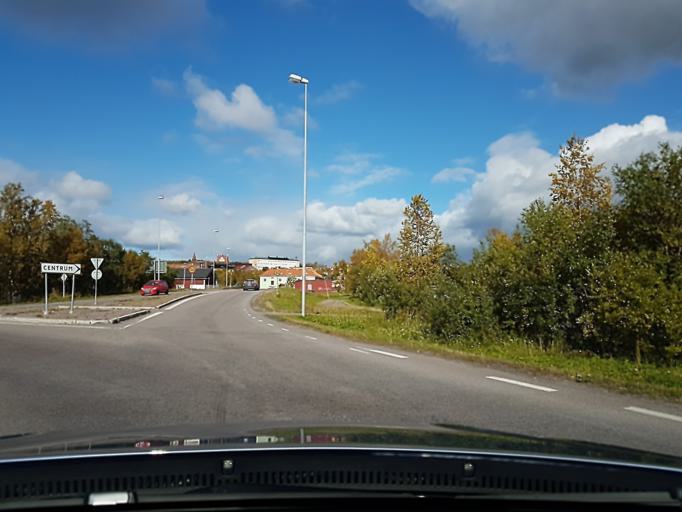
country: SE
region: Norrbotten
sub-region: Kiruna Kommun
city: Kiruna
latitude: 67.8433
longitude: 20.2303
